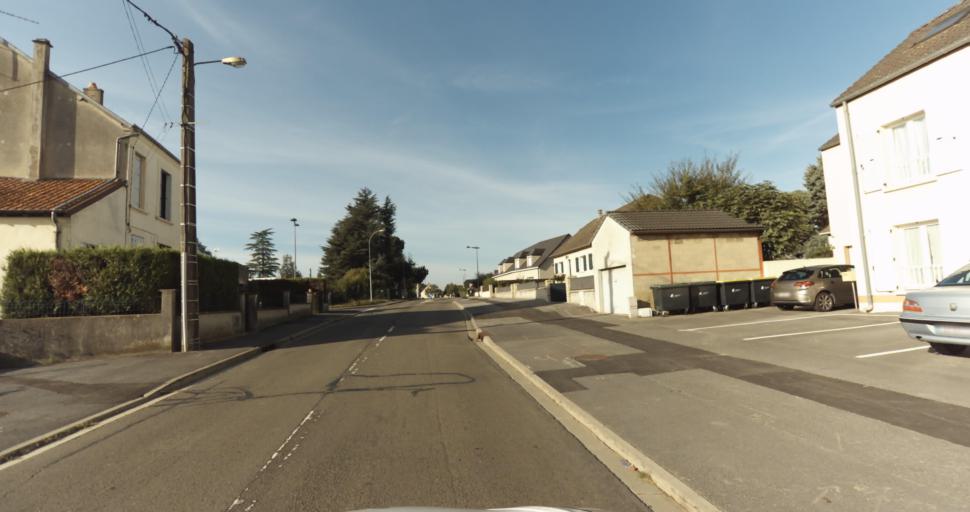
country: FR
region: Champagne-Ardenne
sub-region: Departement des Ardennes
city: Villers-Semeuse
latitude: 49.7377
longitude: 4.7452
